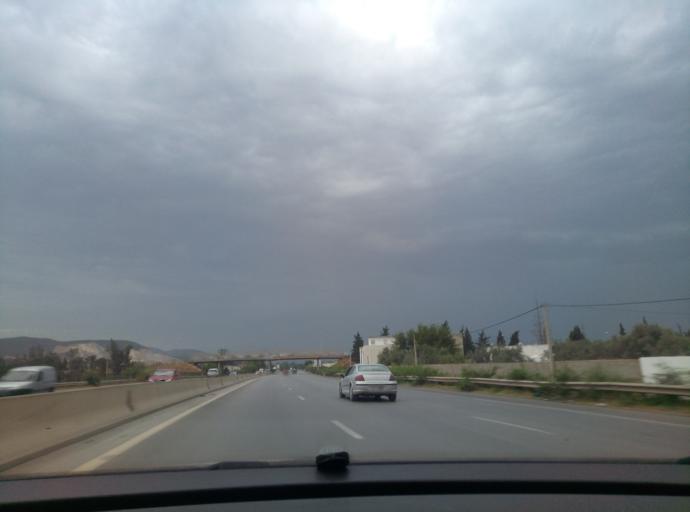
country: TN
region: Tunis
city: La Sebala du Mornag
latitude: 36.7099
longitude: 10.2859
